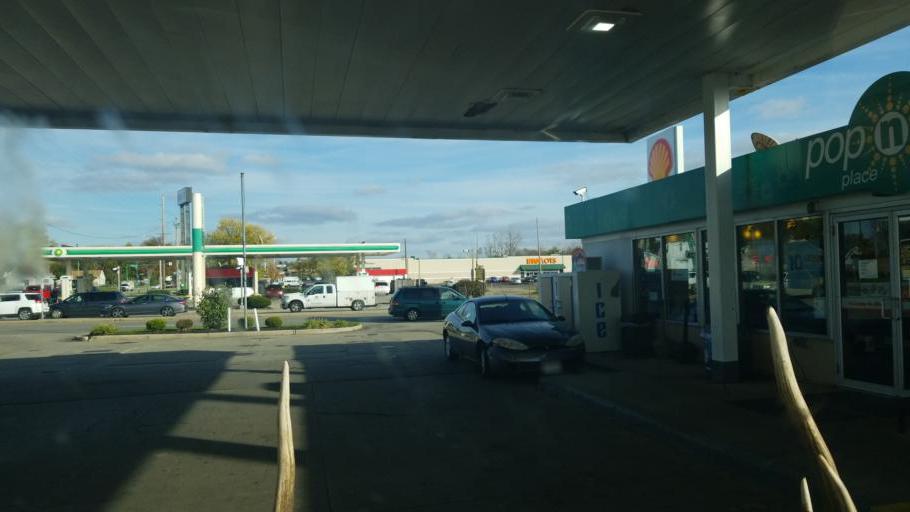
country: US
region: Ohio
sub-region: Clark County
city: Springfield
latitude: 39.8945
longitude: -83.8121
